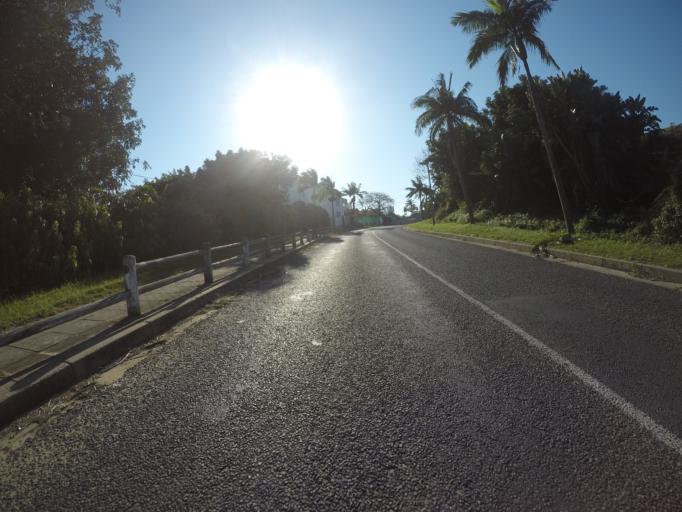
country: ZA
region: KwaZulu-Natal
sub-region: uThungulu District Municipality
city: Richards Bay
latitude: -28.7957
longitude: 32.0964
